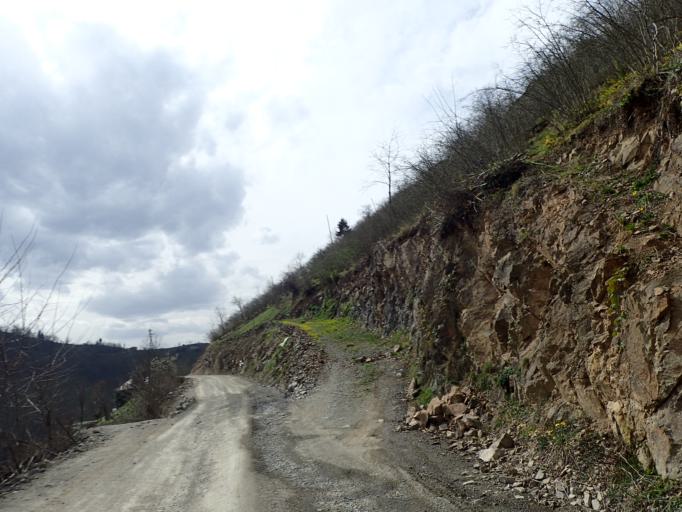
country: TR
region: Ordu
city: Kabaduz
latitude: 40.8141
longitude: 37.8916
